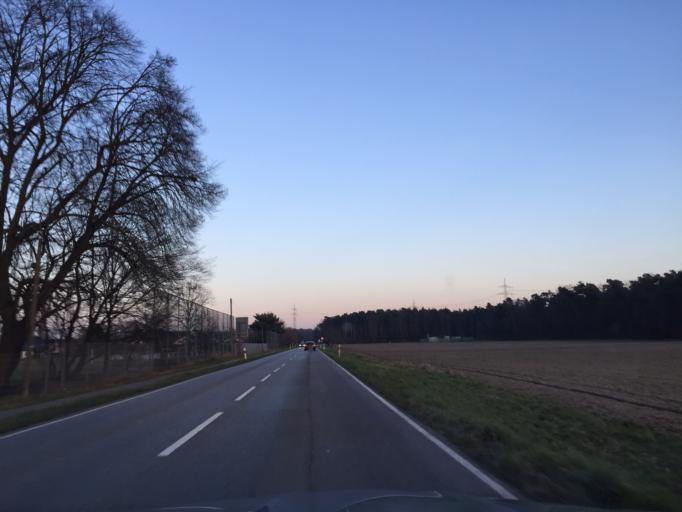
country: DE
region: Baden-Wuerttemberg
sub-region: Karlsruhe Region
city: Reilingen
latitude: 49.2860
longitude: 8.5617
